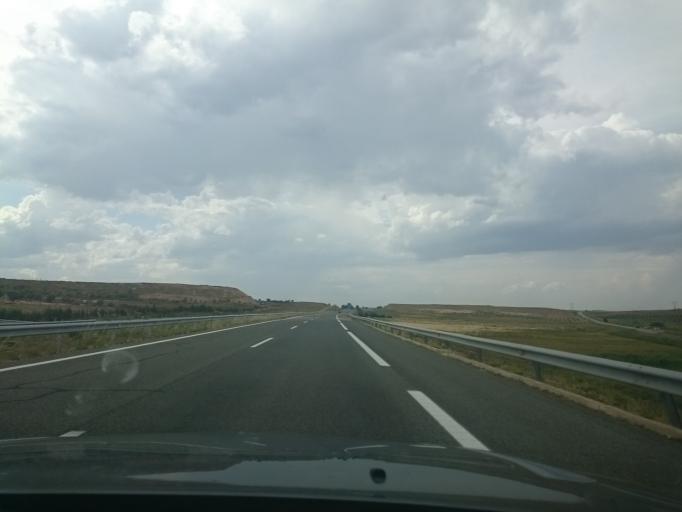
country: ES
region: Navarre
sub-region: Provincia de Navarra
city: Corella
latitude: 42.1579
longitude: -1.8162
